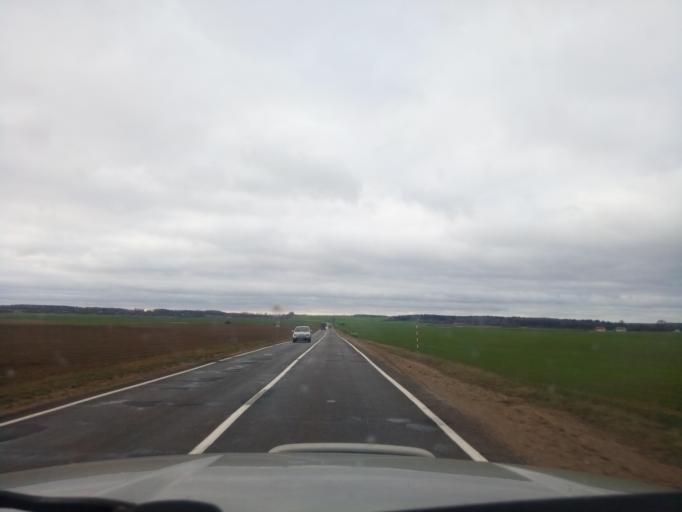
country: BY
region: Minsk
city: Kapyl'
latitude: 53.1971
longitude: 27.2009
